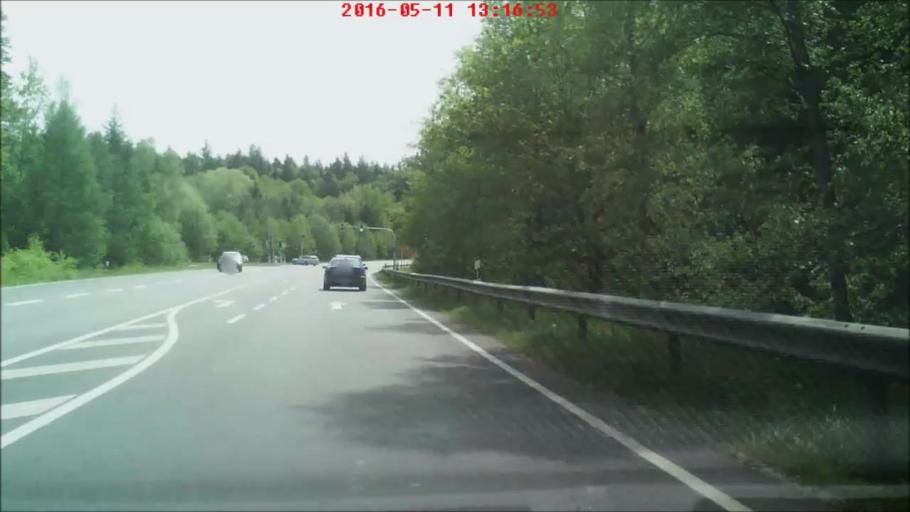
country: DE
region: Bavaria
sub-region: Lower Bavaria
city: Passau
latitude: 48.5433
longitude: 13.4068
